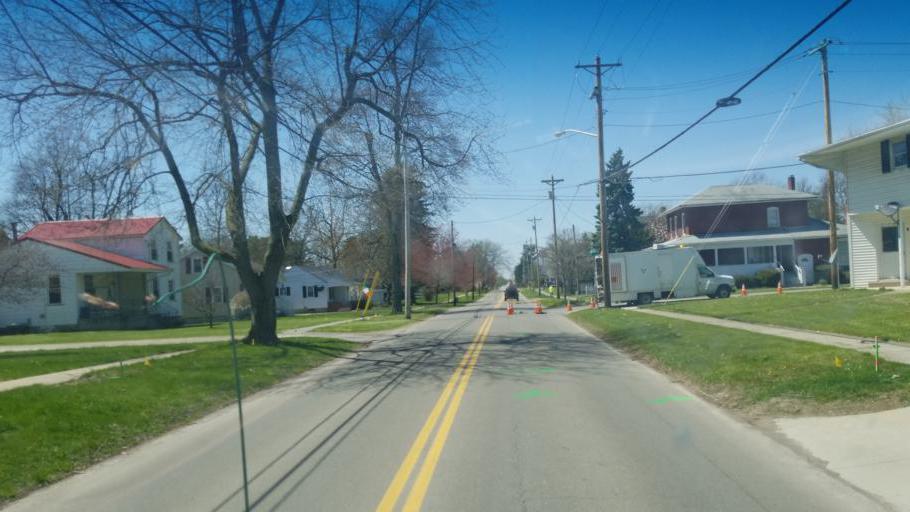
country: US
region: Ohio
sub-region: Huron County
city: New London
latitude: 41.0855
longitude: -82.4030
